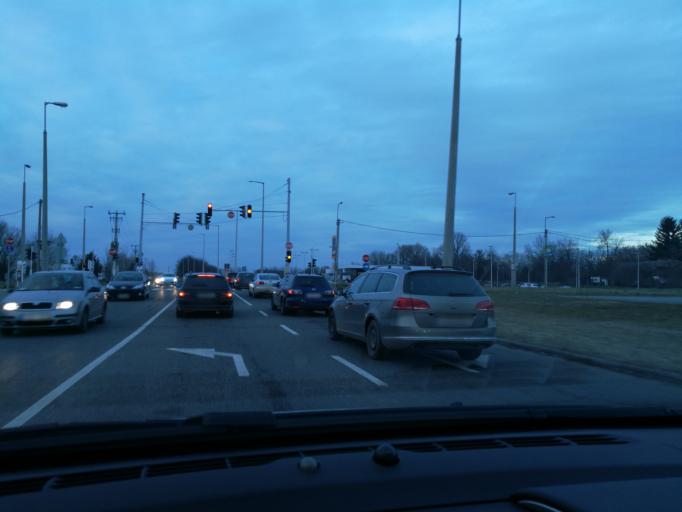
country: HU
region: Szabolcs-Szatmar-Bereg
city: Nyiregyhaza
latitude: 47.9696
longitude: 21.7411
